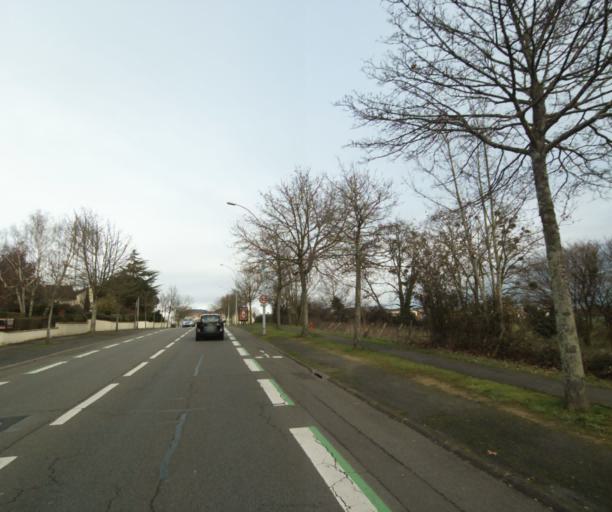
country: FR
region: Pays de la Loire
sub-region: Departement de la Sarthe
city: Sarge-les-le-Mans
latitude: 48.0069
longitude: 0.2278
